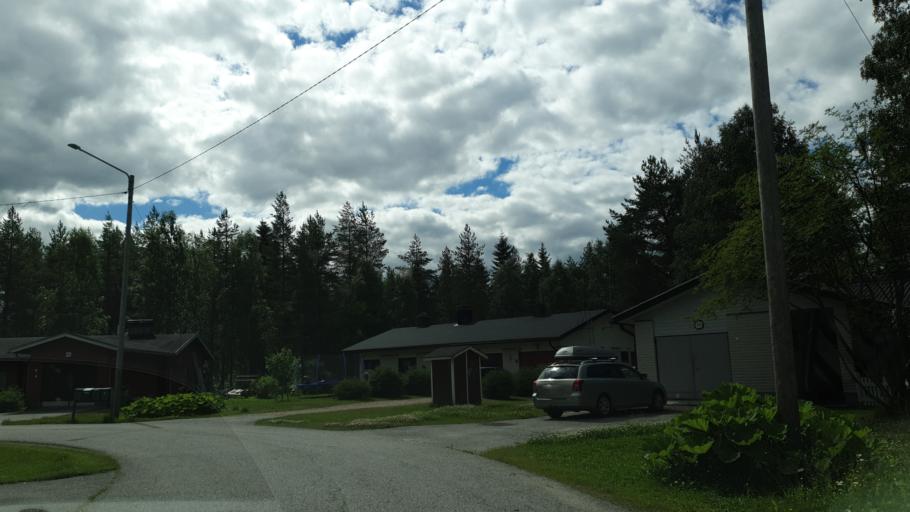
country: FI
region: Kainuu
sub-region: Kehys-Kainuu
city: Kuhmo
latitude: 64.1150
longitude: 29.4784
